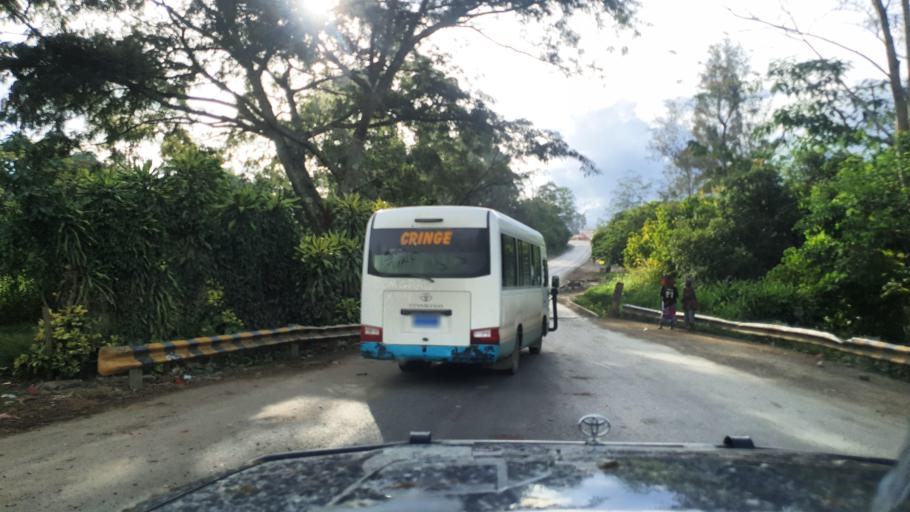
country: PG
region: Jiwaka
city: Minj
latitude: -5.8438
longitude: 144.5858
